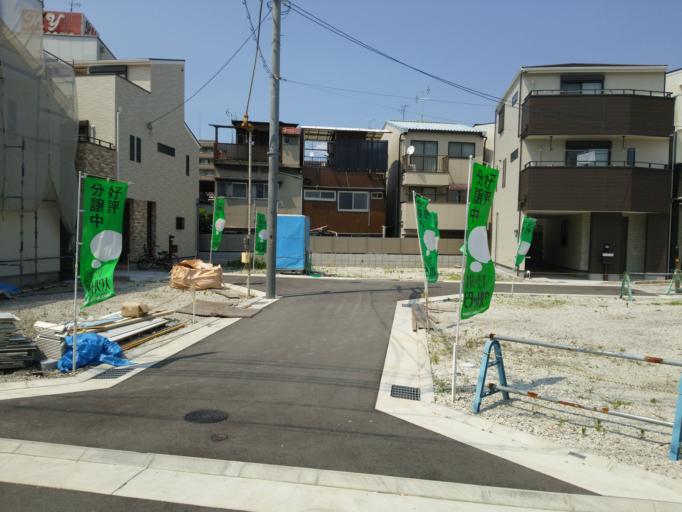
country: JP
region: Hyogo
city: Amagasaki
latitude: 34.7206
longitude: 135.4350
